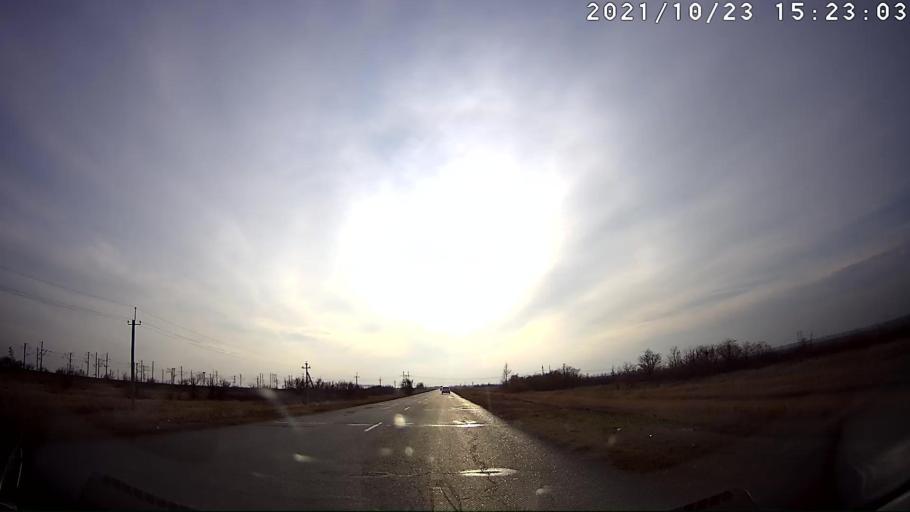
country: RU
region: Volgograd
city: Bereslavka
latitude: 48.3005
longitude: 44.2910
